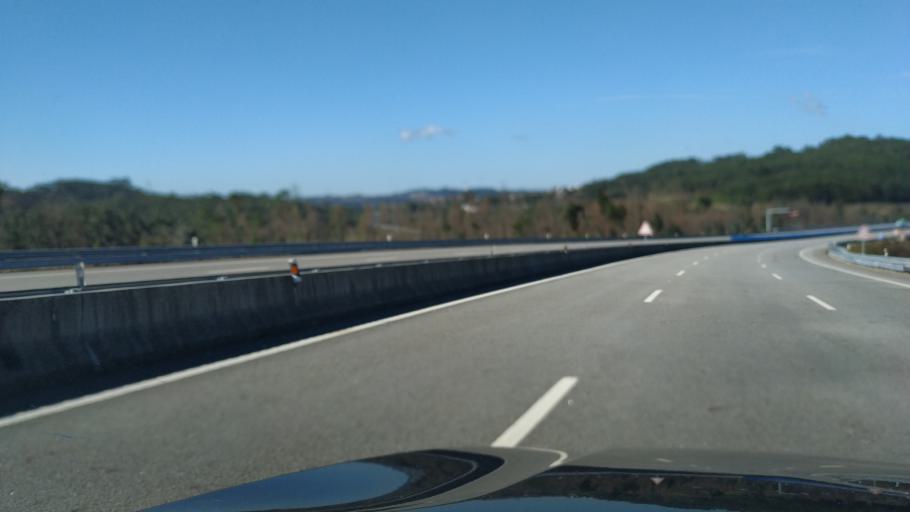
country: PT
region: Porto
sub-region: Vila Nova de Gaia
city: Sandim
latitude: 41.0298
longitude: -8.4861
